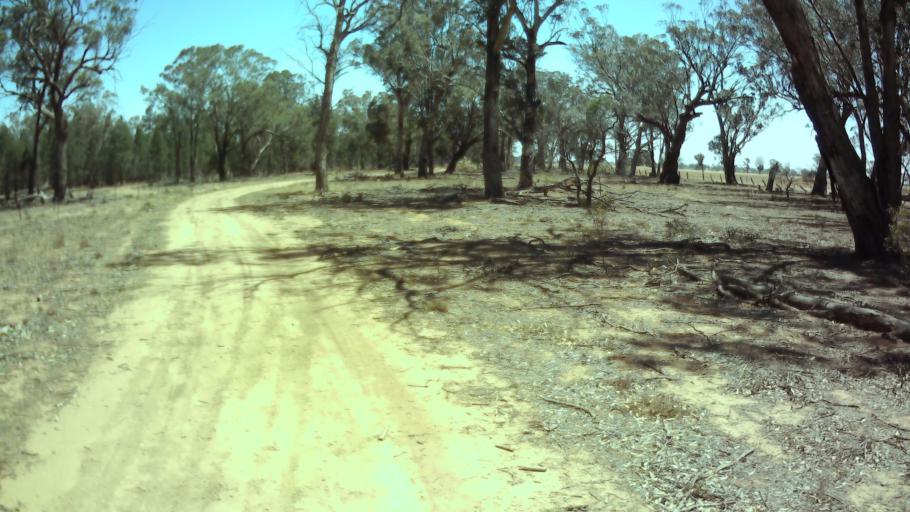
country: AU
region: New South Wales
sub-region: Weddin
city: Grenfell
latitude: -34.0608
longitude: 147.8111
